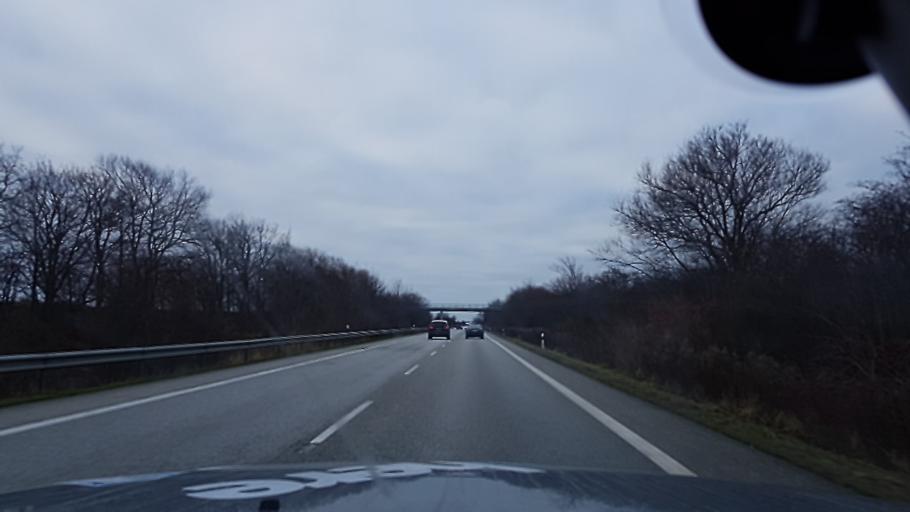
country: DE
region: Schleswig-Holstein
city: Fehmarn
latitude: 54.4714
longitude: 11.2040
